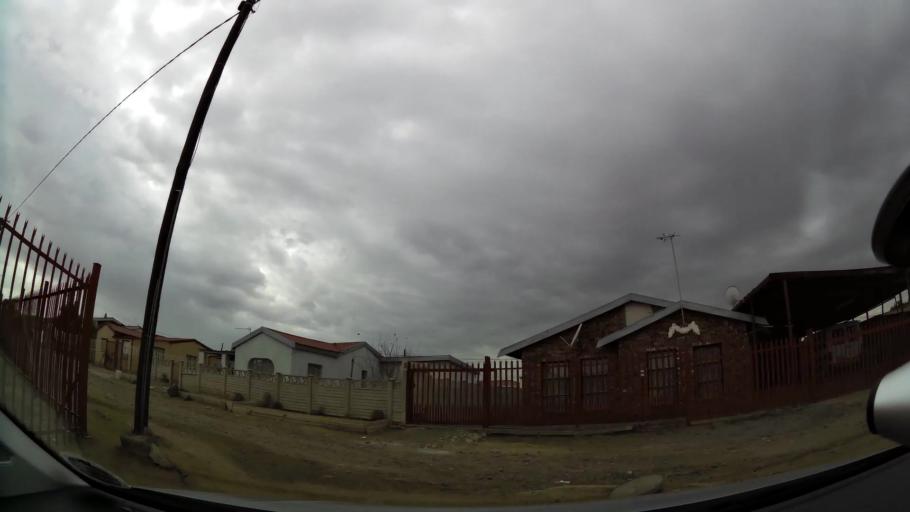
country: ZA
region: Orange Free State
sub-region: Fezile Dabi District Municipality
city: Kroonstad
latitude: -27.6486
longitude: 27.2074
